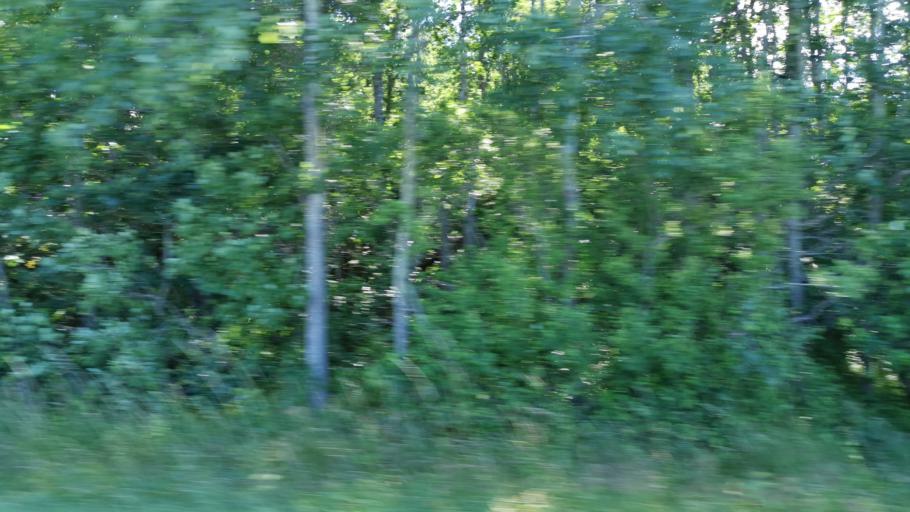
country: SE
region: Vaestra Goetaland
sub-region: Lysekils Kommun
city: Lysekil
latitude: 58.2345
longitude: 11.4564
